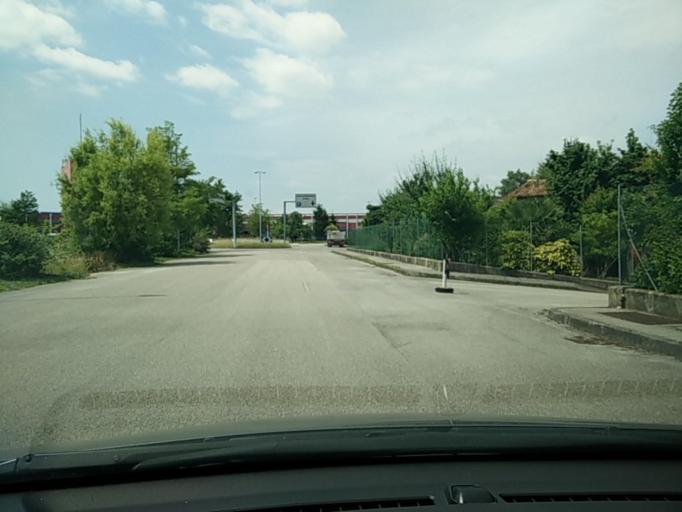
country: IT
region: Veneto
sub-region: Provincia di Venezia
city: Zelarino
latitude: 45.5187
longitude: 12.2440
